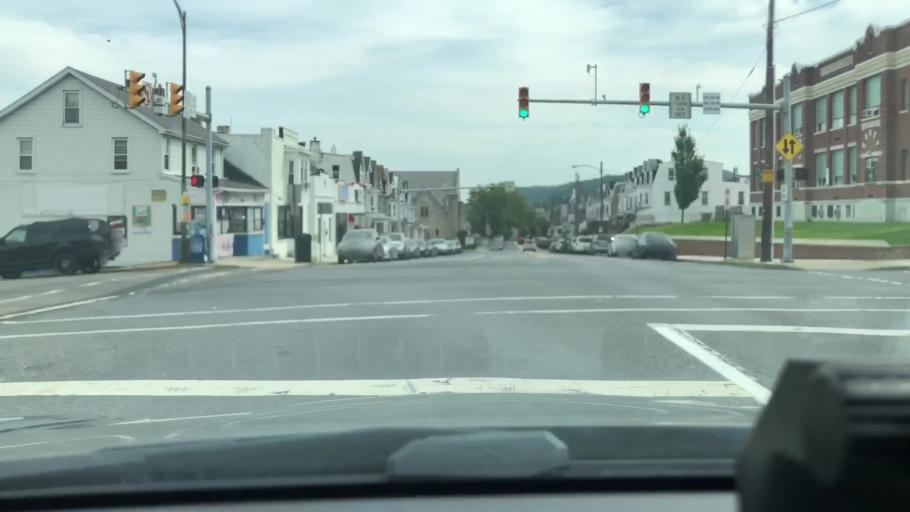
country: US
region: Pennsylvania
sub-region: Lehigh County
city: Allentown
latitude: 40.5915
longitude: -75.4692
